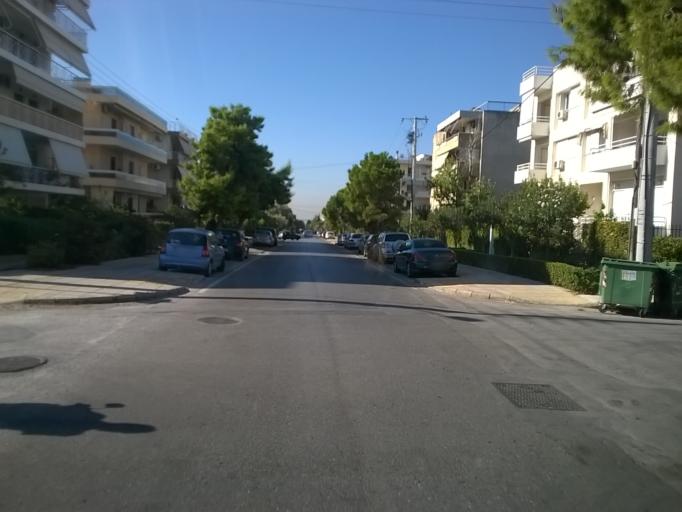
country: GR
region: Attica
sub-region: Nomarchia Athinas
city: Glyfada
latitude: 37.8738
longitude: 23.7561
